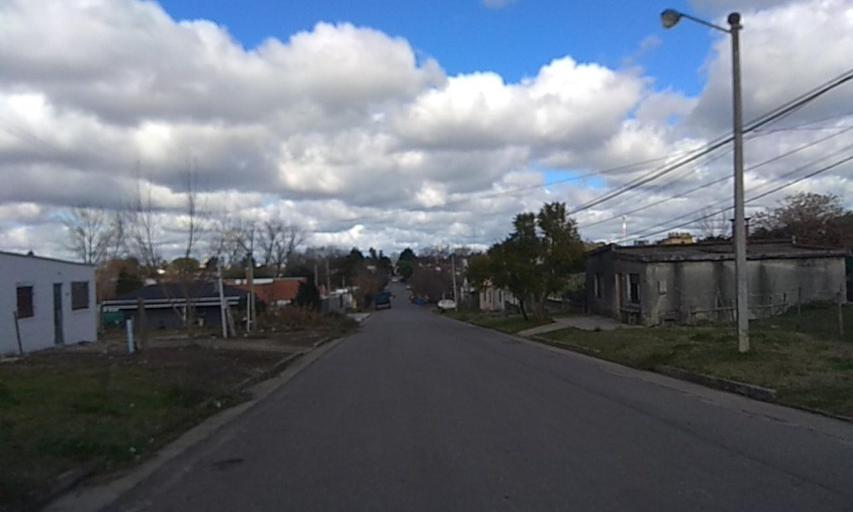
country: UY
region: Florida
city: Florida
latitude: -34.0911
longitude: -56.2278
